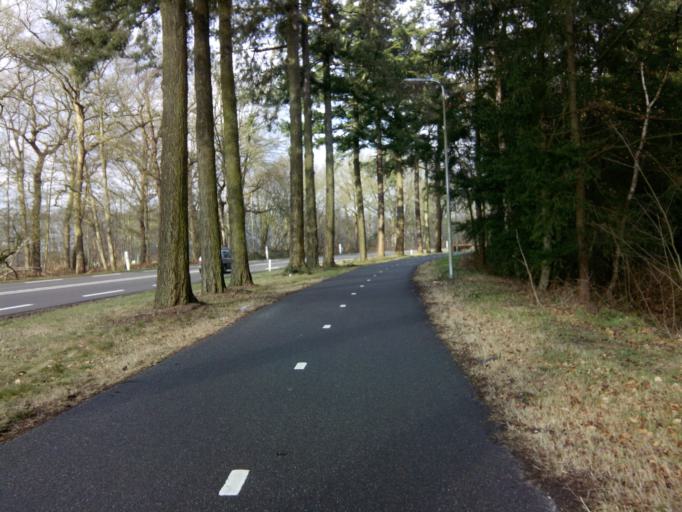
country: NL
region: Utrecht
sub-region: Gemeente Utrechtse Heuvelrug
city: Maarsbergen
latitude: 52.0489
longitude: 5.4029
